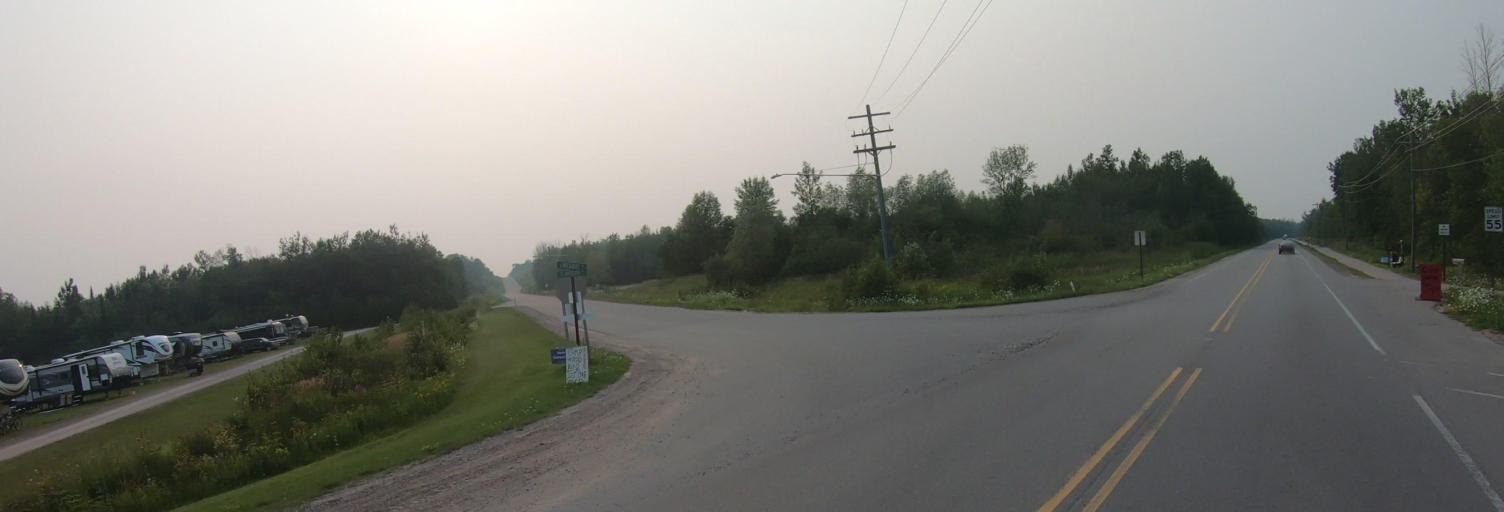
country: US
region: Michigan
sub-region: Chippewa County
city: Sault Ste. Marie
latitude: 46.4256
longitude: -84.6049
